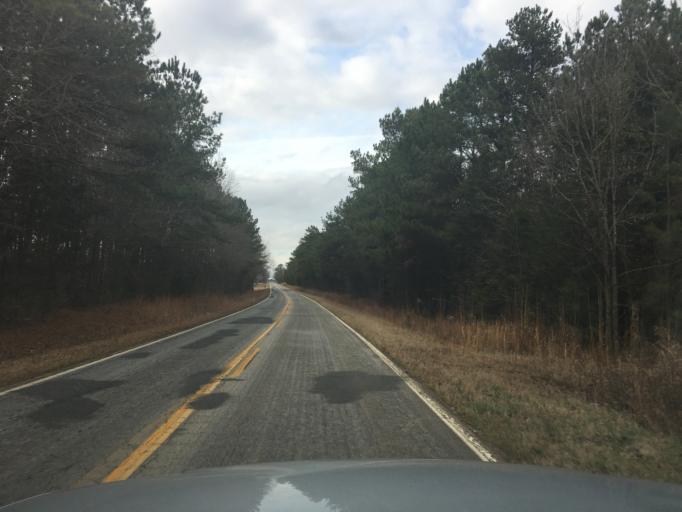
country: US
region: South Carolina
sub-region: Abbeville County
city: Due West
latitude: 34.3120
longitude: -82.4592
